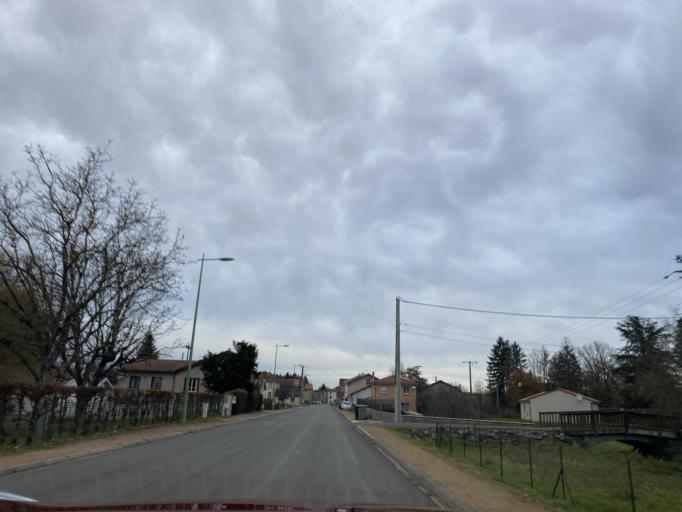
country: FR
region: Auvergne
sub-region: Departement du Puy-de-Dome
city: Peschadoires
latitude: 45.8357
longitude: 3.4997
